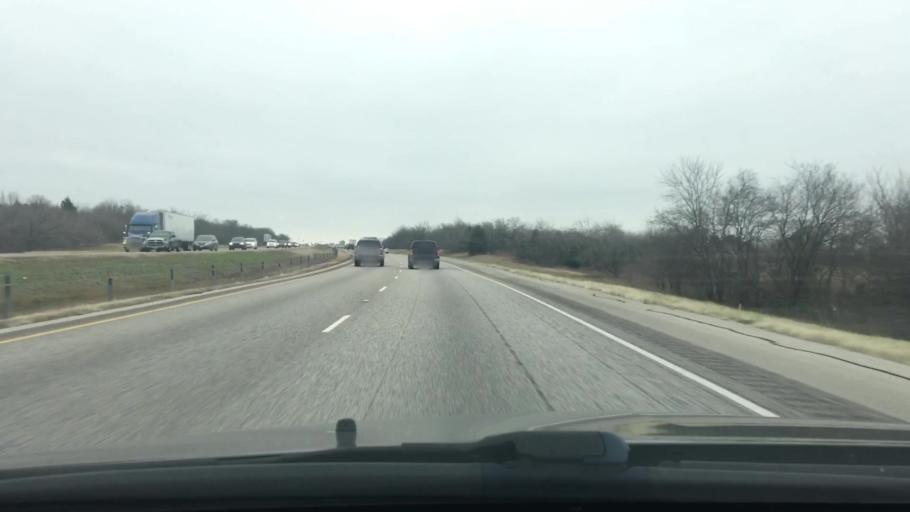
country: US
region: Texas
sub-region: Freestone County
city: Wortham
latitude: 31.8692
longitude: -96.3344
